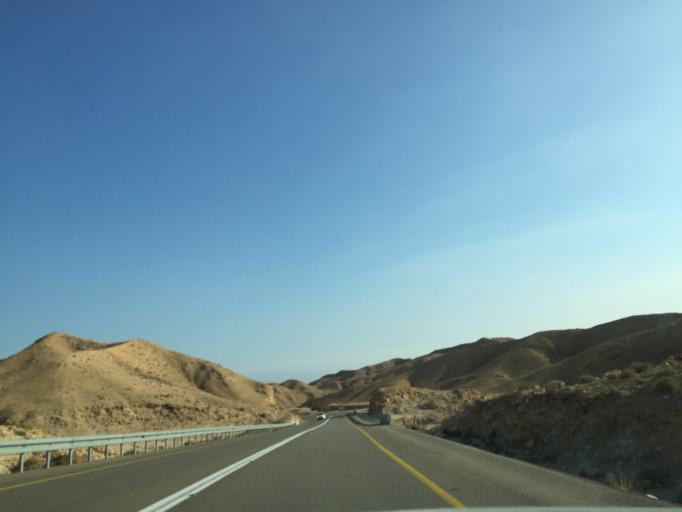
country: IL
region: Southern District
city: `En Boqeq
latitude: 31.1927
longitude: 35.2794
